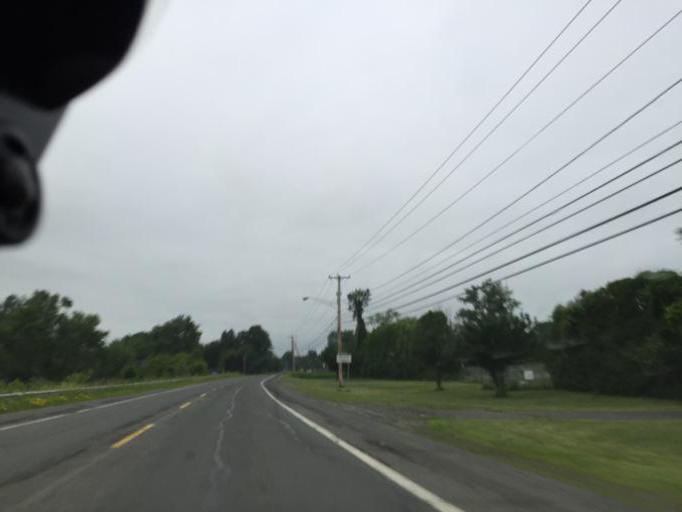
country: US
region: Massachusetts
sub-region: Berkshire County
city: Sheffield
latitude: 42.1408
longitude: -73.3631
